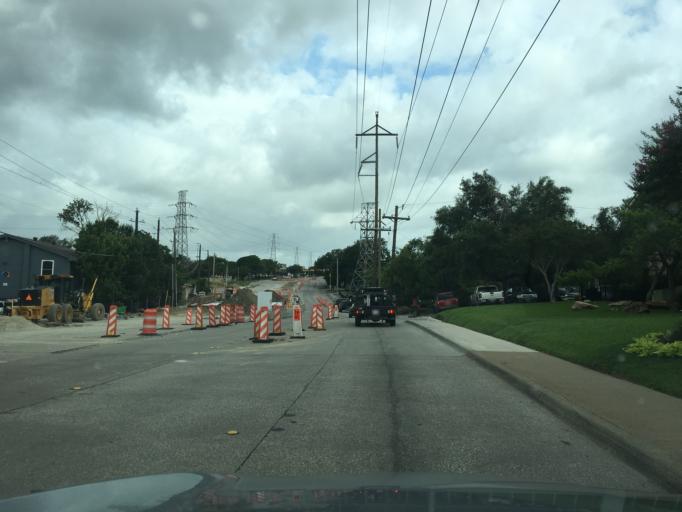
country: US
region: Texas
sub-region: Dallas County
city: Richardson
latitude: 32.9401
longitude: -96.7594
